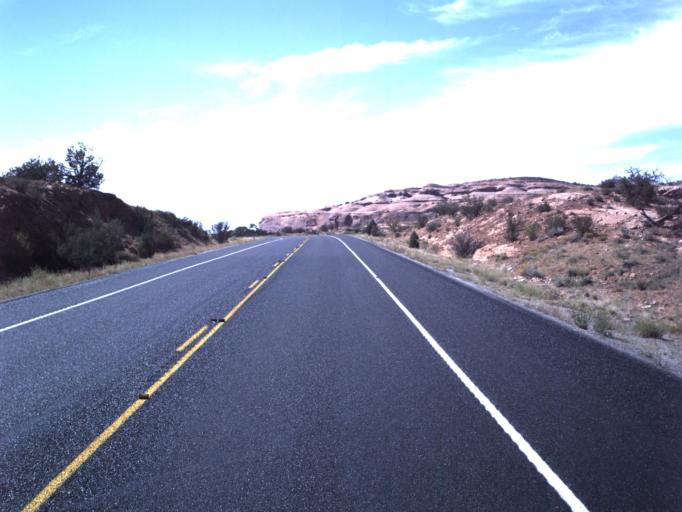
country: US
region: Utah
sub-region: Grand County
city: Moab
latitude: 38.6361
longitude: -109.7834
